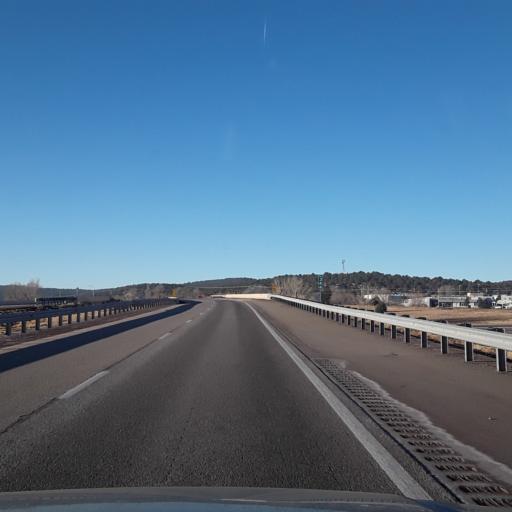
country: US
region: New Mexico
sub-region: San Miguel County
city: Las Vegas
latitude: 35.5701
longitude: -105.2192
